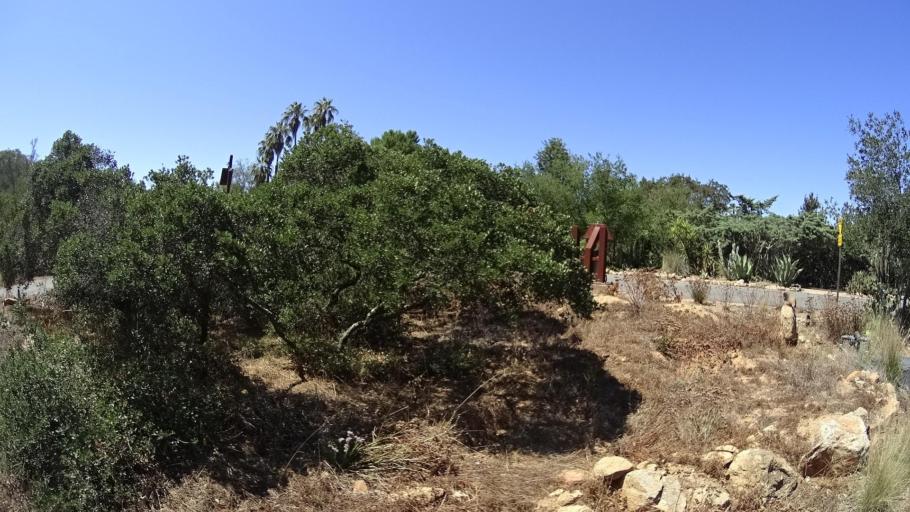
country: US
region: California
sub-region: San Diego County
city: Rainbow
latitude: 33.3878
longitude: -117.1306
